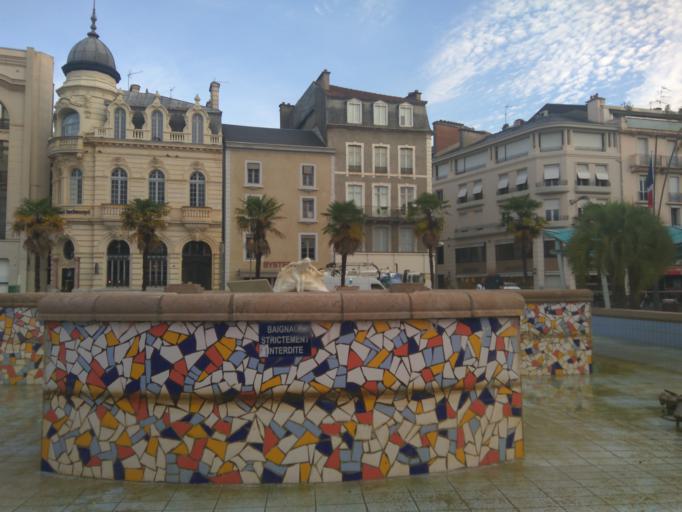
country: FR
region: Aquitaine
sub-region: Departement des Pyrenees-Atlantiques
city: Pau
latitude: 43.2959
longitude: -0.3686
